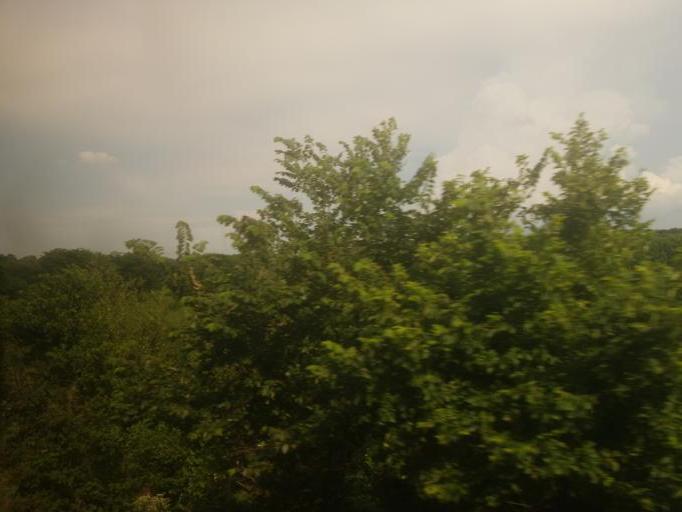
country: US
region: Illinois
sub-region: Henry County
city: Galva
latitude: 41.1063
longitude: -90.1731
